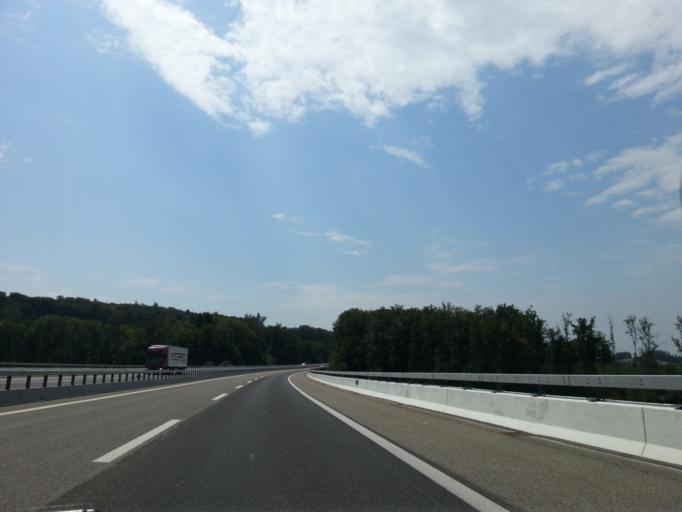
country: CH
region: Fribourg
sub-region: See District
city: Kerzers
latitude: 46.9505
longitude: 7.1650
